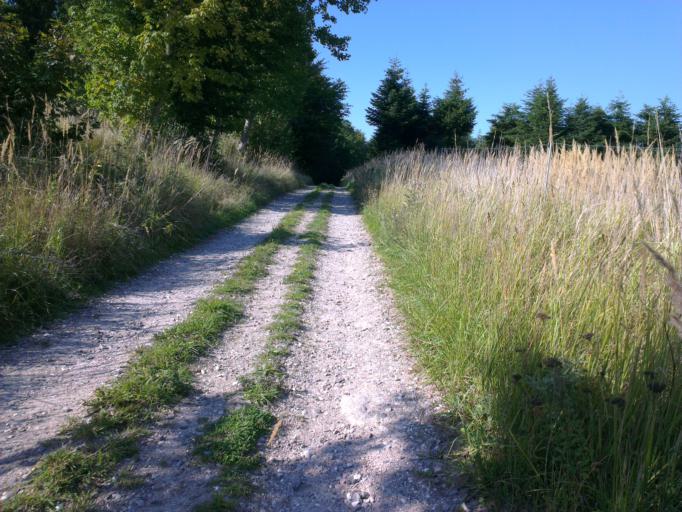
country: DK
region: Capital Region
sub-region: Frederikssund Kommune
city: Frederikssund
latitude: 55.8385
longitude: 12.0291
